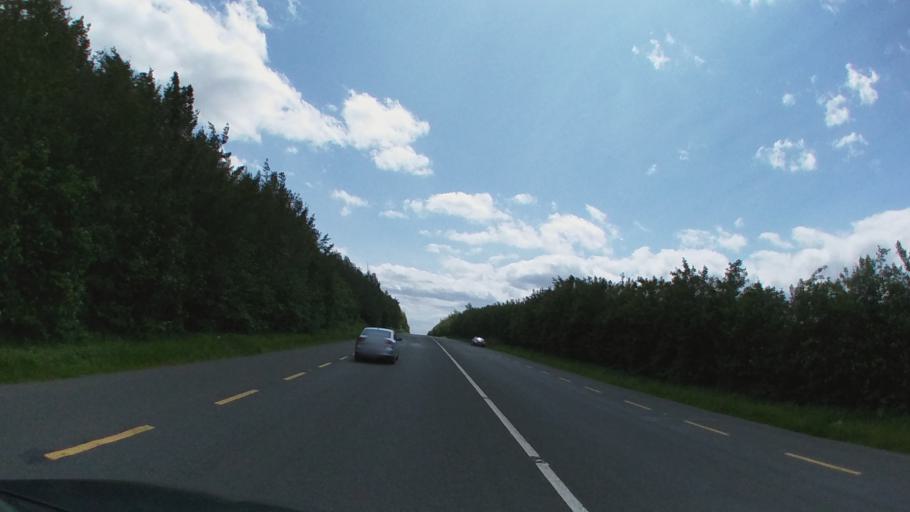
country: IE
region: Leinster
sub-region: Kildare
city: Moone
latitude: 53.0137
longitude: -6.8018
